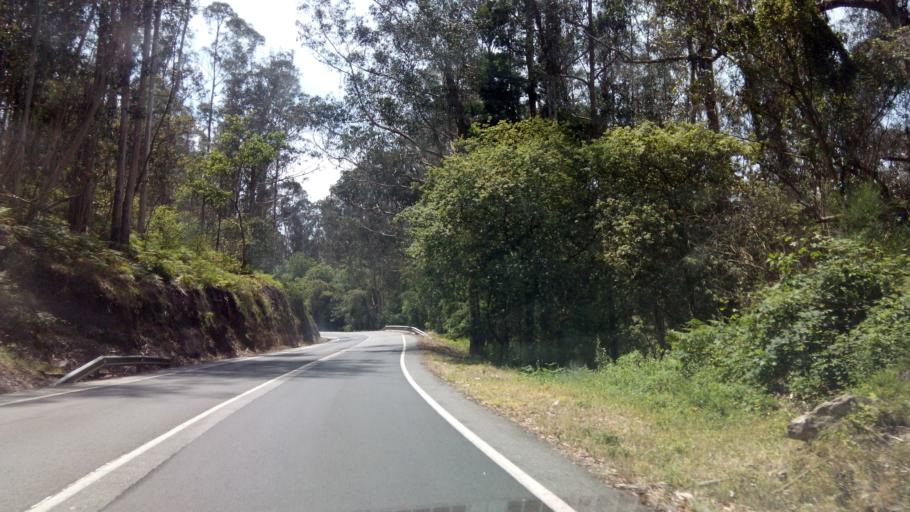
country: ES
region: Galicia
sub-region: Provincia de Pontevedra
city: Marin
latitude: 42.3404
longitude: -8.7105
